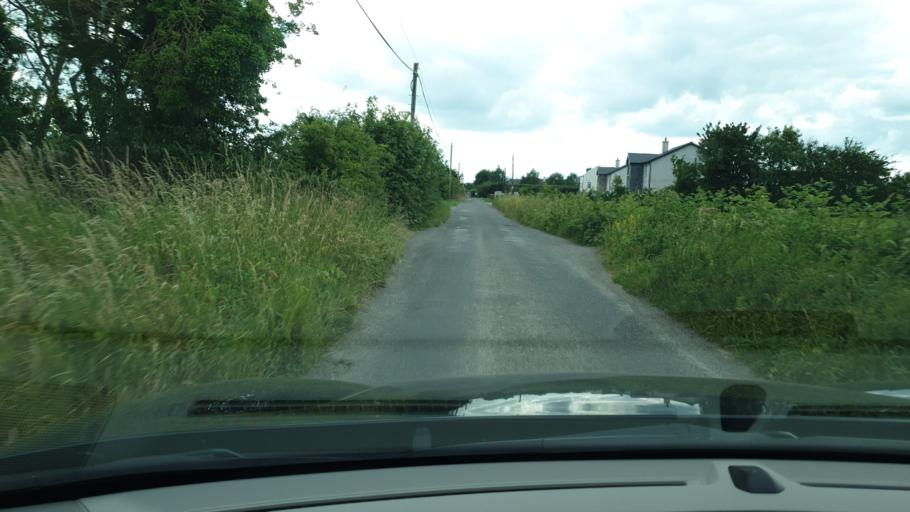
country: IE
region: Leinster
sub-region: An Mhi
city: Ashbourne
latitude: 53.4681
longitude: -6.3731
